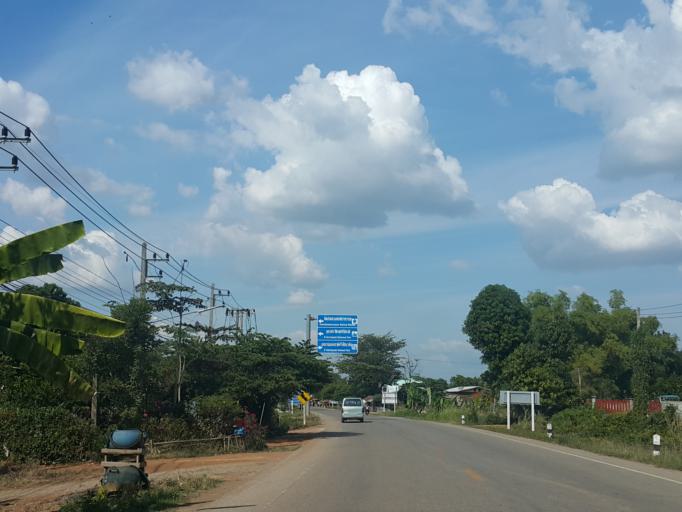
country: TH
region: Sukhothai
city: Sawankhalok
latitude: 17.2984
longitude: 99.8266
